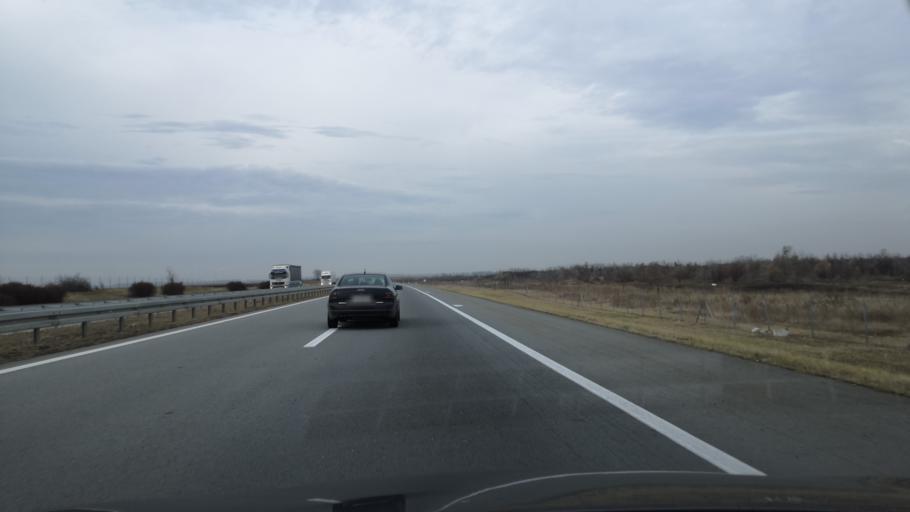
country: RS
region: Autonomna Pokrajina Vojvodina
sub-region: Juznobacki Okrug
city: Kovilj
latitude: 45.2592
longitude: 19.9958
